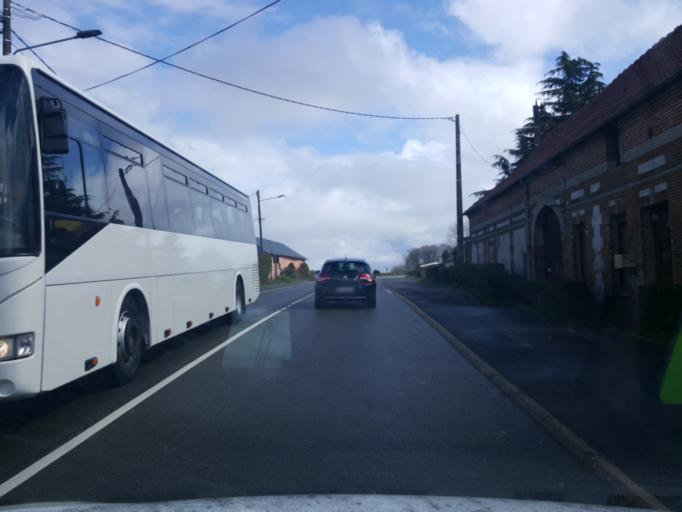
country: FR
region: Picardie
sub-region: Departement de l'Oise
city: Auneuil
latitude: 49.3570
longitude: 1.9485
